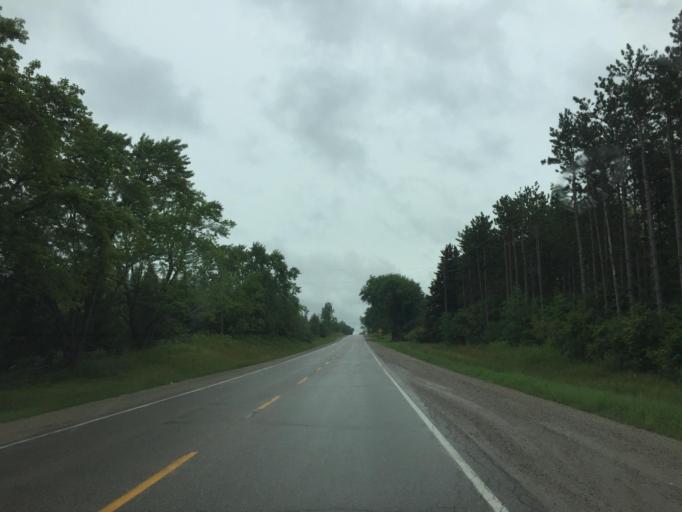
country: CA
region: Ontario
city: Cambridge
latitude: 43.4372
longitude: -80.2632
